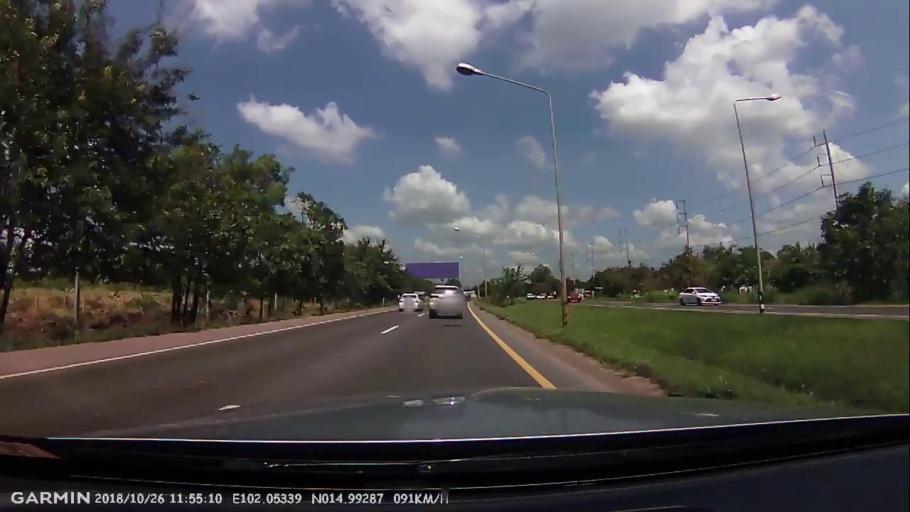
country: TH
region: Nakhon Ratchasima
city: Nakhon Ratchasima
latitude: 14.9930
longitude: 102.0534
